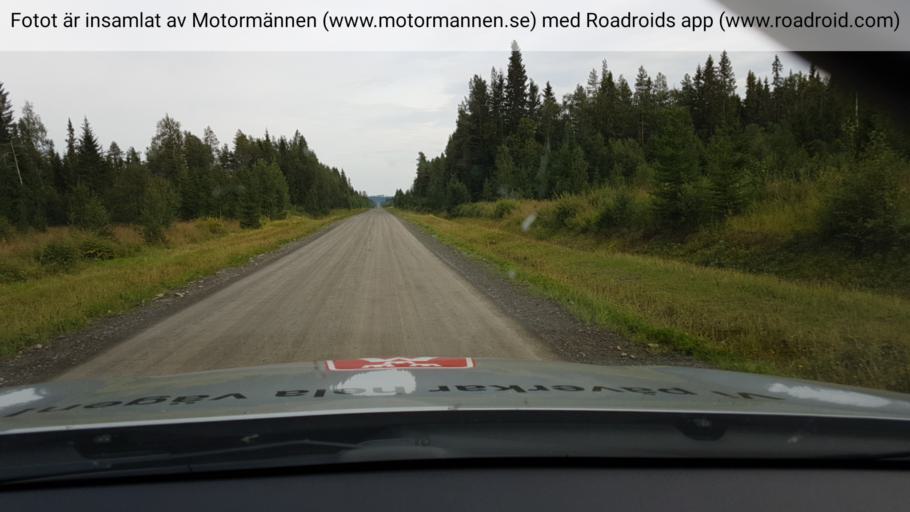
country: SE
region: Jaemtland
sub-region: OEstersunds Kommun
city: Lit
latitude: 63.6739
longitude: 14.8776
